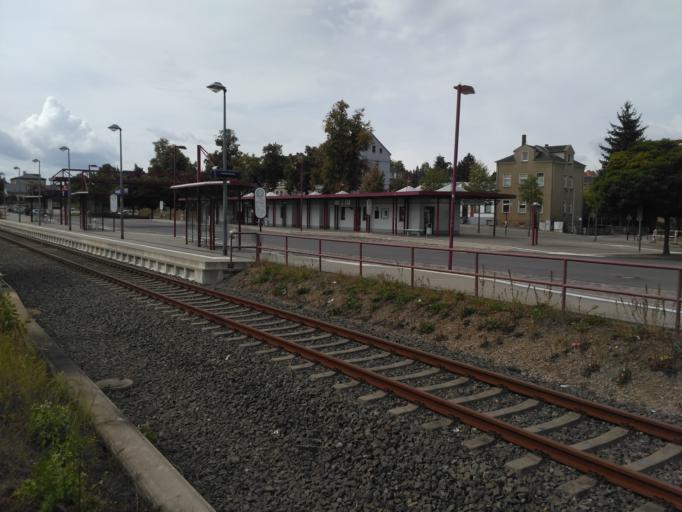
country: DE
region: Saxony
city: Burgstadt
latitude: 50.9160
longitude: 12.8129
